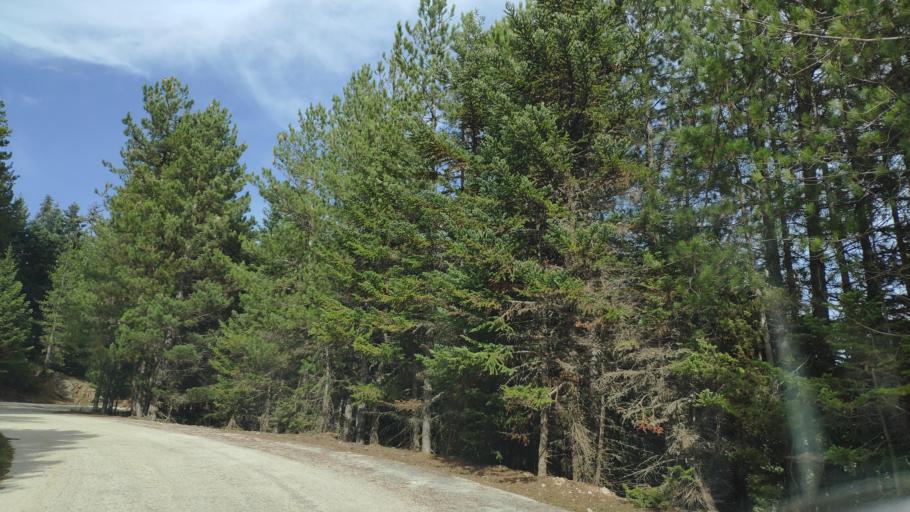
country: GR
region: West Greece
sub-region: Nomos Achaias
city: Aiyira
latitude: 38.0274
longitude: 22.3889
